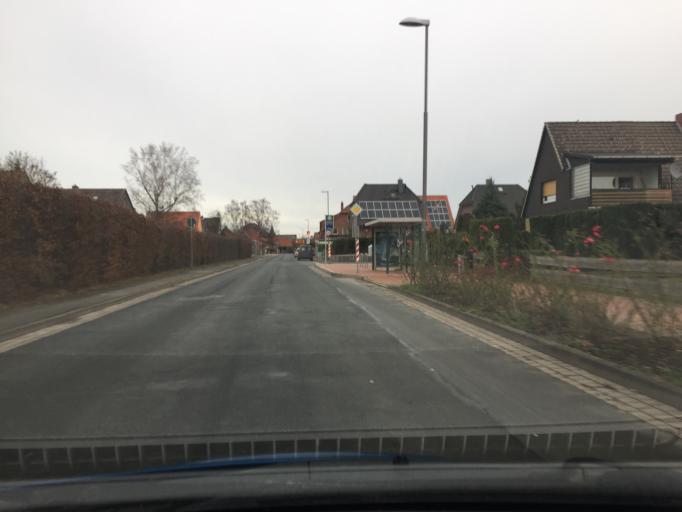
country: DE
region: Lower Saxony
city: Pattensen
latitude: 52.2877
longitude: 9.7664
